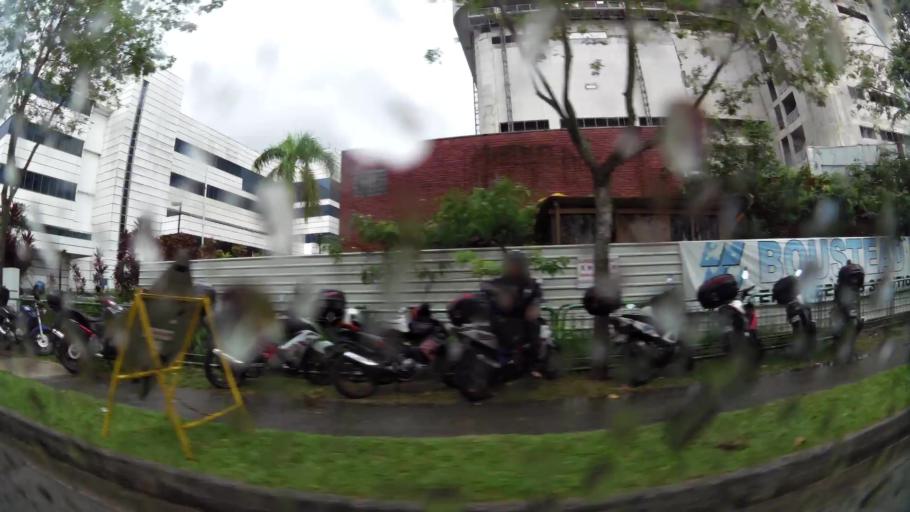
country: MY
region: Johor
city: Kampung Pasir Gudang Baru
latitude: 1.3895
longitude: 103.8457
